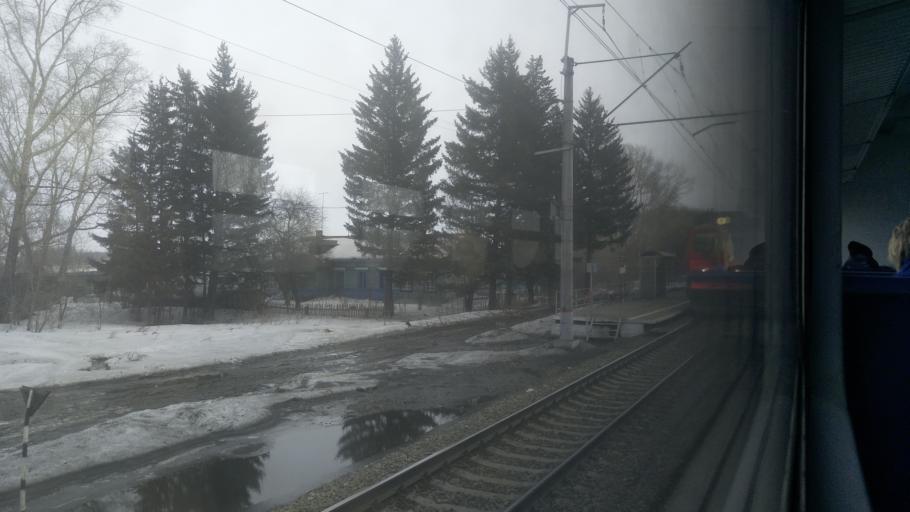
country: RU
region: Kemerovo
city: Yurga
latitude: 55.6986
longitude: 84.6527
